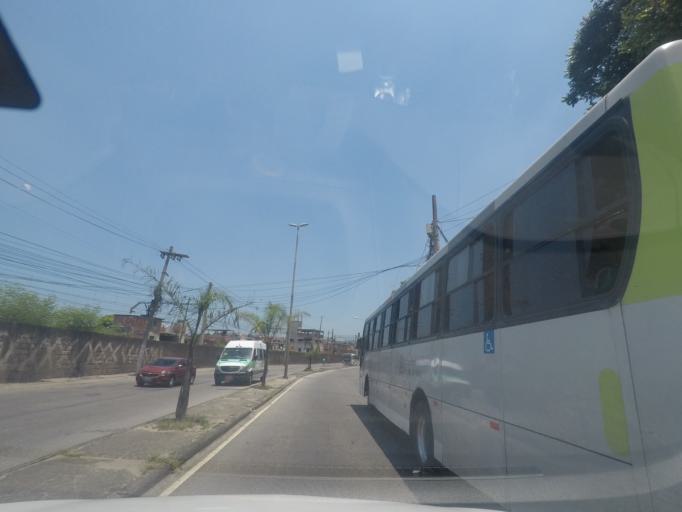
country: BR
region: Rio de Janeiro
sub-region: Duque De Caxias
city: Duque de Caxias
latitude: -22.8099
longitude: -43.3019
